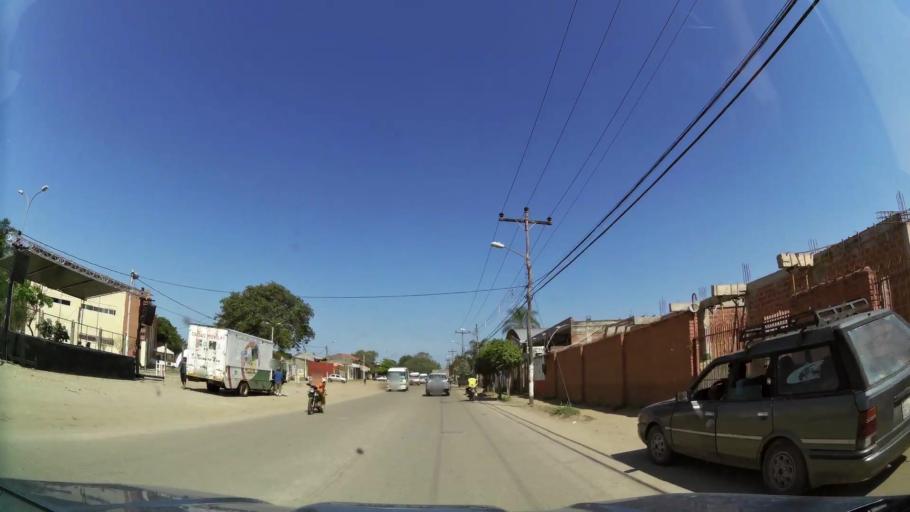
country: BO
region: Santa Cruz
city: Santa Cruz de la Sierra
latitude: -17.7490
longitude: -63.1221
